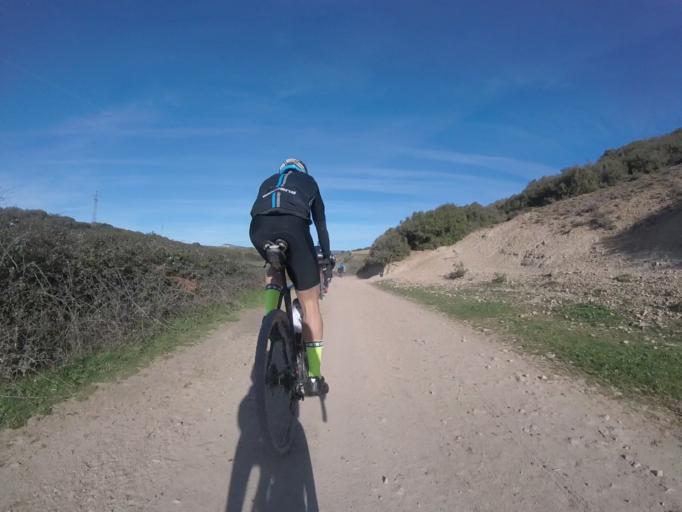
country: ES
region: Navarre
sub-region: Provincia de Navarra
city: Yerri
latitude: 42.6996
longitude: -1.9655
